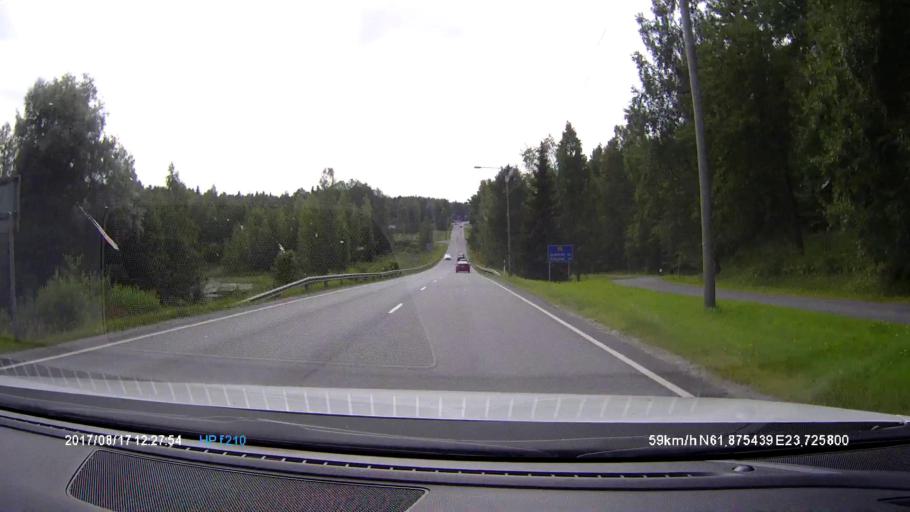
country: FI
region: Pirkanmaa
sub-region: Tampere
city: Kuru
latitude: 61.8750
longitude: 23.7259
